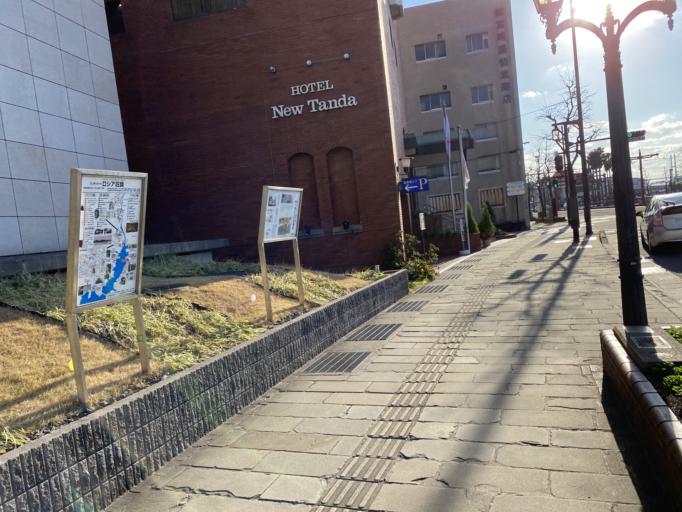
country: JP
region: Nagasaki
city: Nagasaki-shi
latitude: 32.7394
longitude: 129.8718
